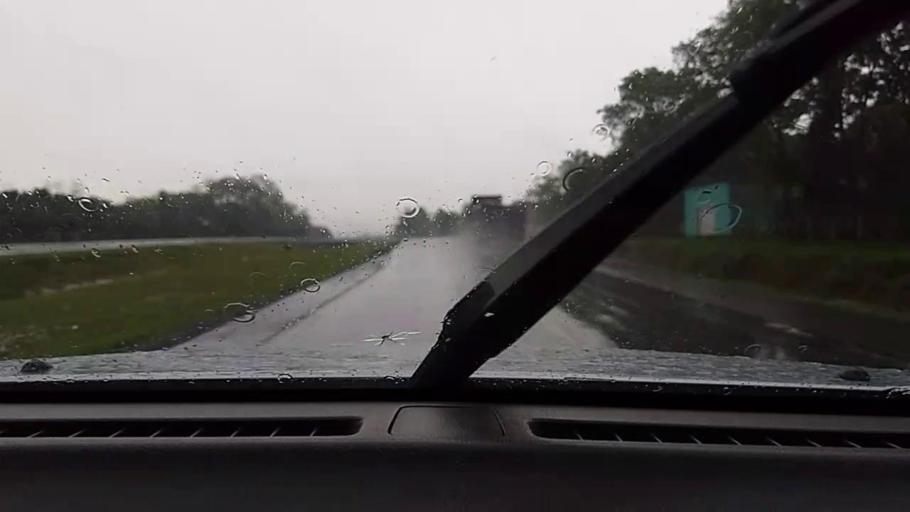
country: PY
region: Caaguazu
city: Repatriacion
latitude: -25.4461
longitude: -55.8863
